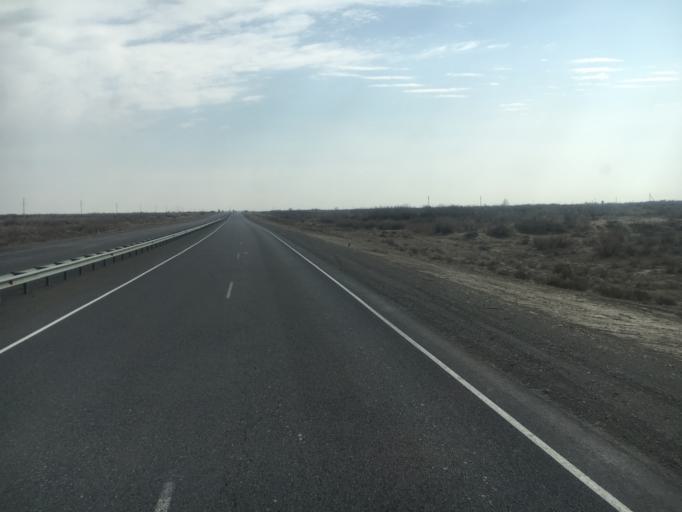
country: KZ
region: Qyzylorda
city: Belkol
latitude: 44.6532
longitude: 66.0295
